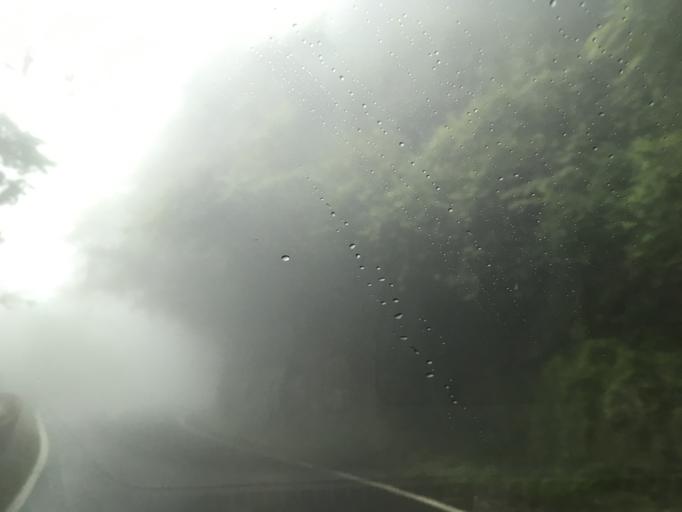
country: TW
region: Taiwan
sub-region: Hualien
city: Hualian
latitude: 24.1898
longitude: 121.4201
